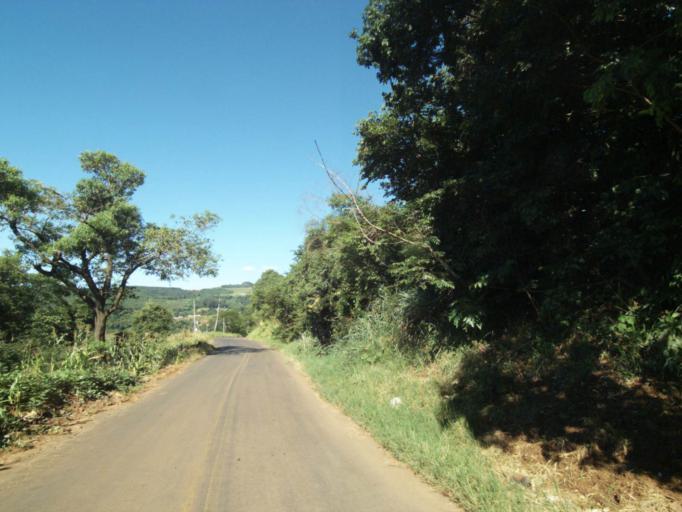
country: BR
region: Parana
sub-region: Ampere
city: Ampere
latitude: -26.1712
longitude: -53.3689
